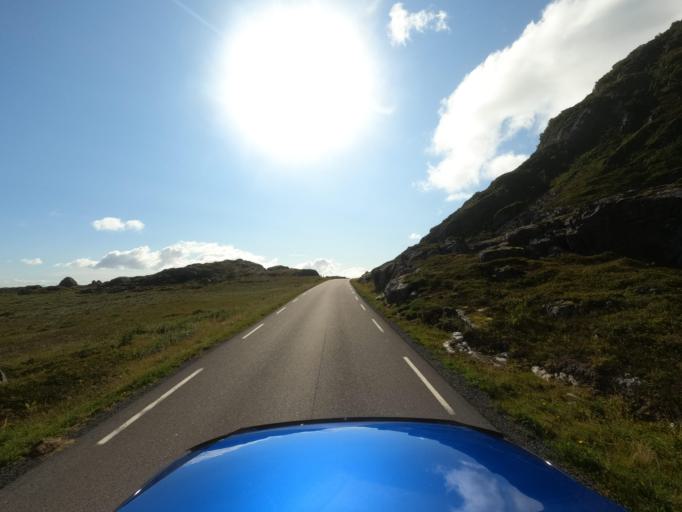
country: NO
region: Nordland
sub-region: Vestvagoy
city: Evjen
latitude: 68.1990
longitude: 14.0362
